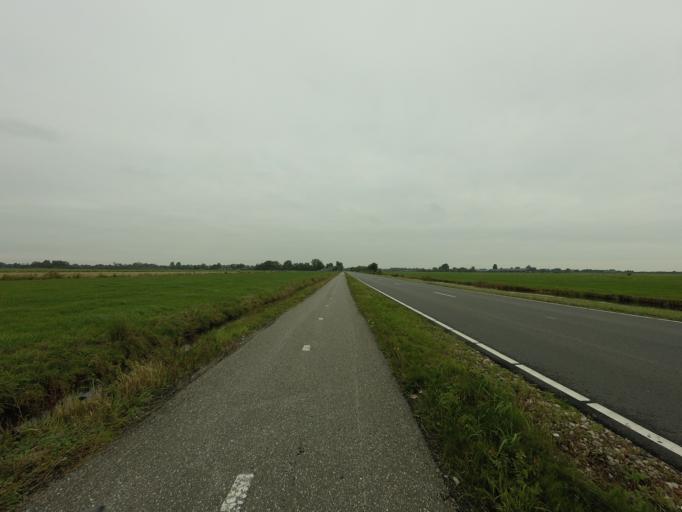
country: NL
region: Utrecht
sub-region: Gemeente Woerden
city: Woerden
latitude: 52.1417
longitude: 4.8608
